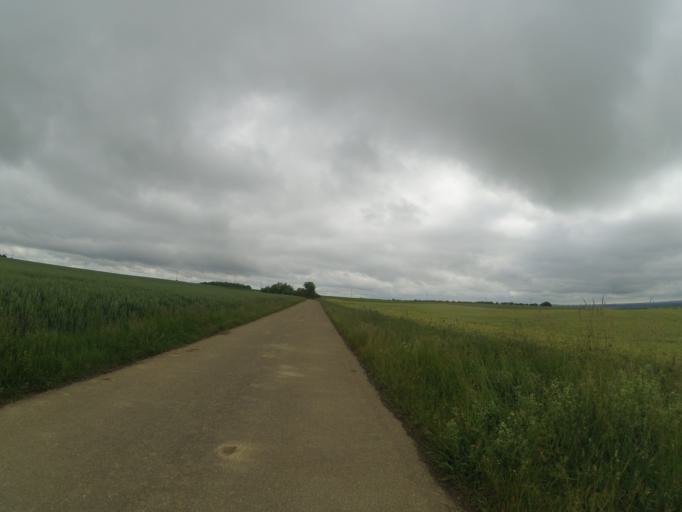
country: DE
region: Baden-Wuerttemberg
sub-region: Tuebingen Region
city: Bernstadt
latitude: 48.4723
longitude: 10.0541
